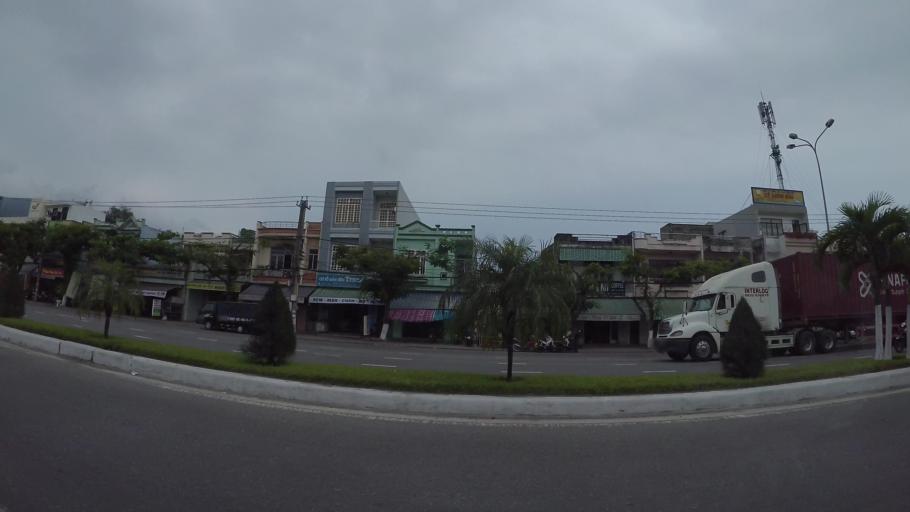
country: VN
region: Da Nang
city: Da Nang
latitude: 16.1009
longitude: 108.2472
